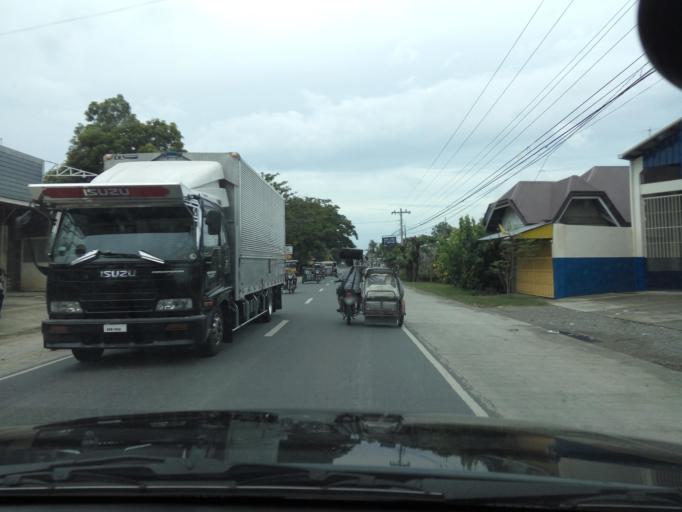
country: PH
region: Central Luzon
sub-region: Province of Nueva Ecija
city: Concepcion
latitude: 15.4486
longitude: 120.8041
